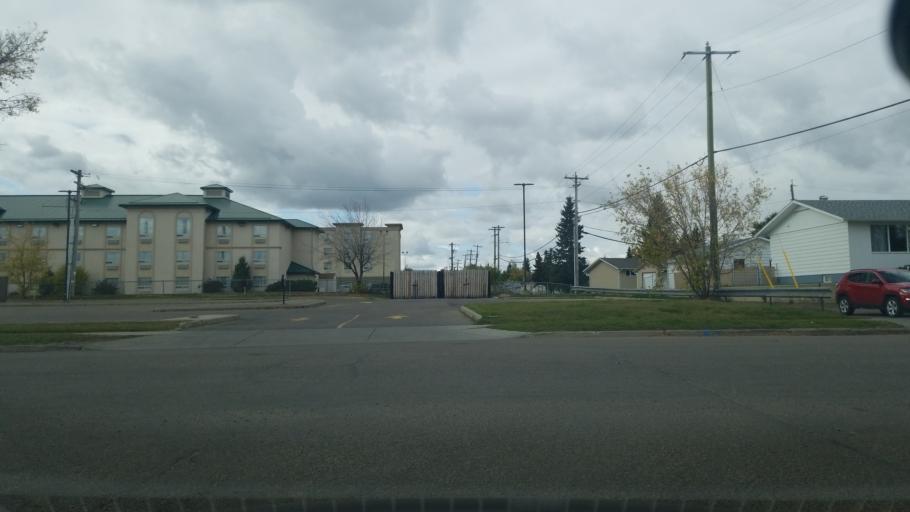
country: CA
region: Saskatchewan
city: Lloydminster
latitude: 53.2790
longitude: -110.0196
